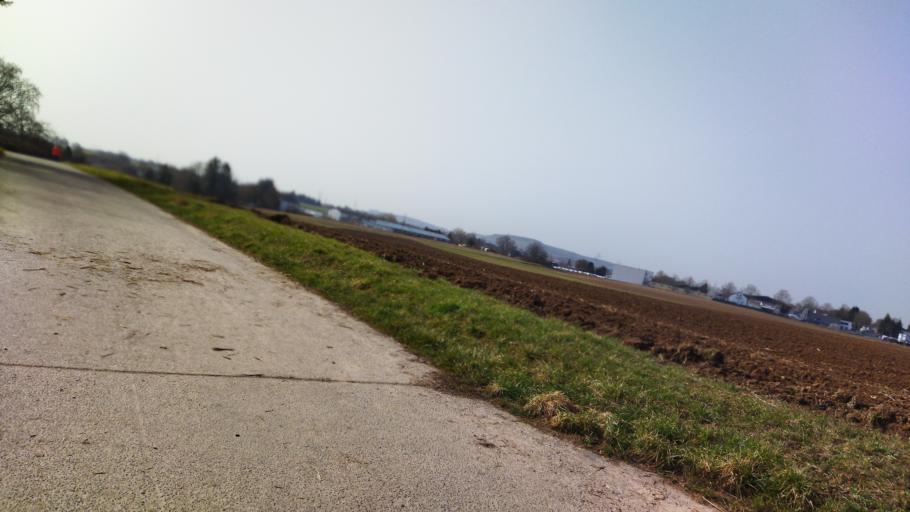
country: DE
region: Baden-Wuerttemberg
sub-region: Regierungsbezirk Stuttgart
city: Heilbronn
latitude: 49.1422
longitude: 9.1747
